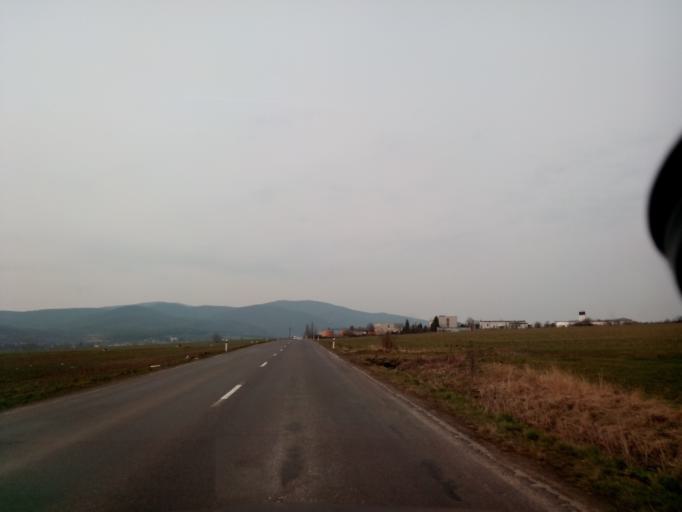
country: SK
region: Kosicky
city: Secovce
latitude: 48.6324
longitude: 21.5838
